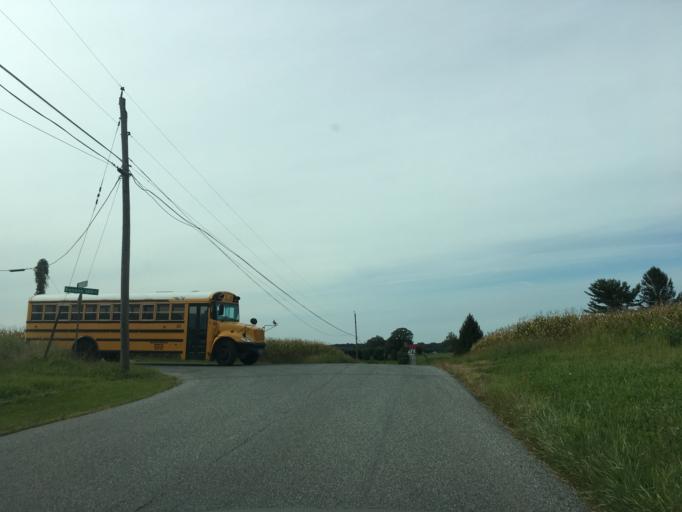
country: US
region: Maryland
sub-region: Baltimore County
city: Hunt Valley
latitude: 39.5788
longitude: -76.7133
